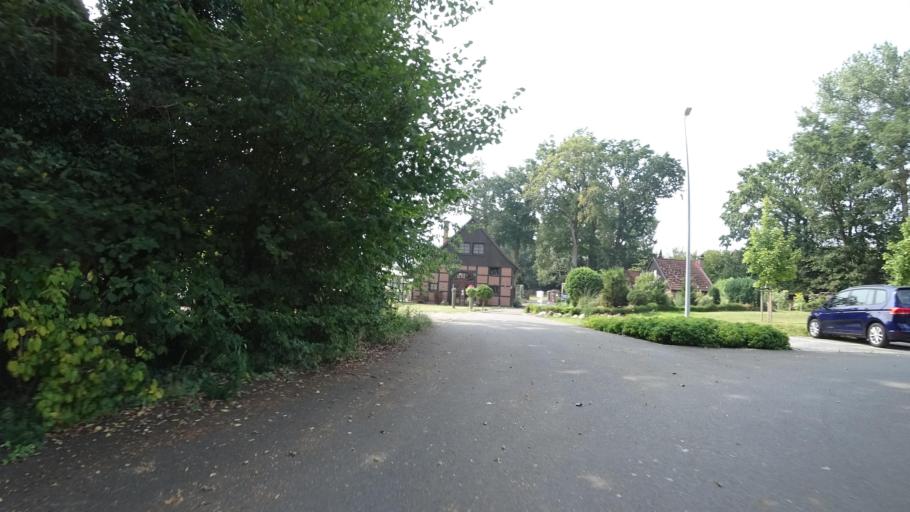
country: DE
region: North Rhine-Westphalia
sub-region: Regierungsbezirk Detmold
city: Guetersloh
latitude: 51.9296
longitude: 8.4240
